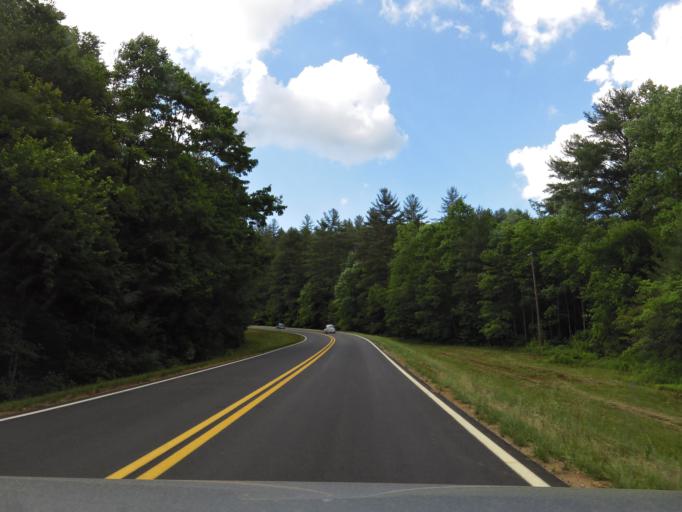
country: US
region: Georgia
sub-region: Towns County
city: Hiawassee
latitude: 34.8483
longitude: -83.7782
